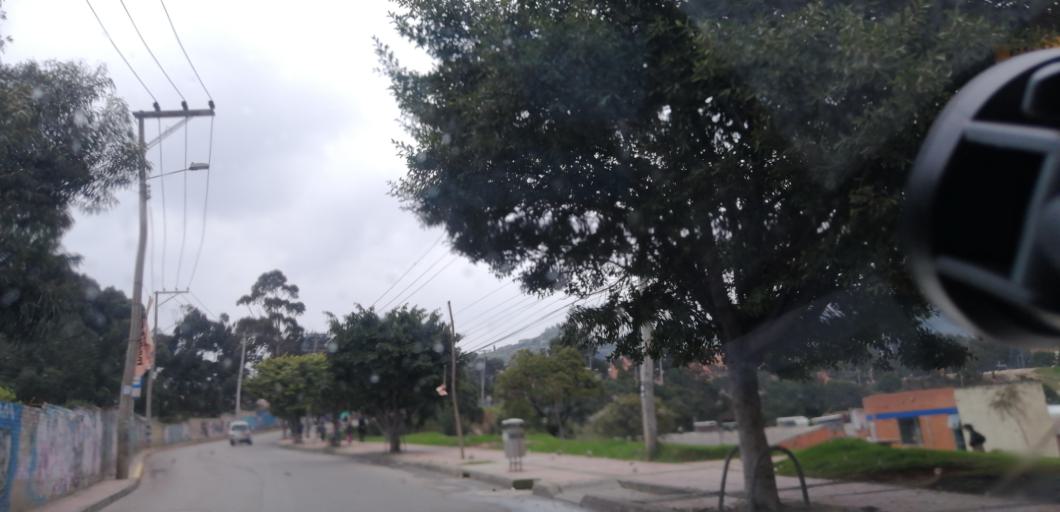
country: CO
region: Bogota D.C.
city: Bogota
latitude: 4.5346
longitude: -74.1180
